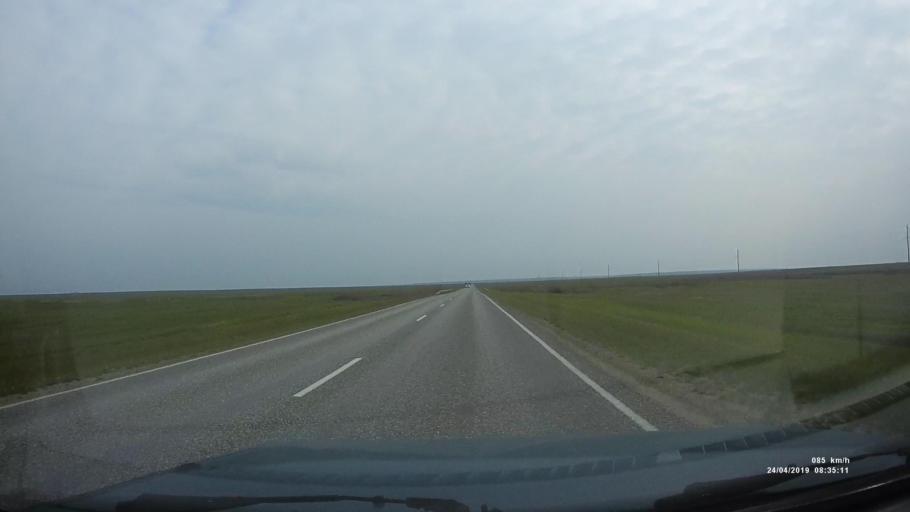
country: RU
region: Kalmykiya
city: Arshan'
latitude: 46.1958
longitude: 43.9156
